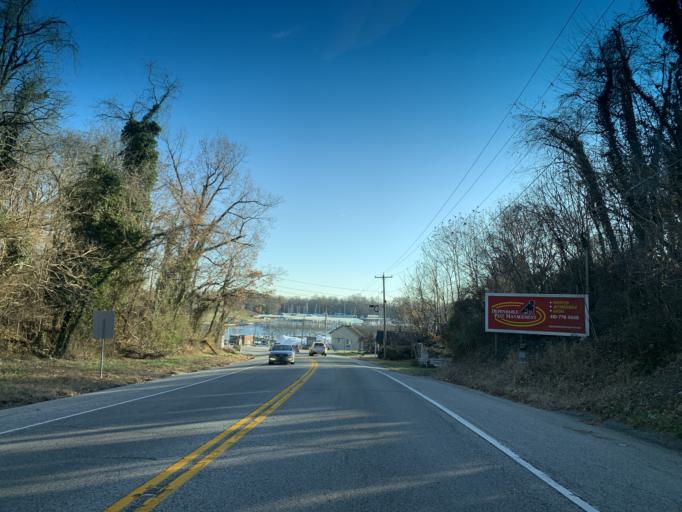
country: US
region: Delaware
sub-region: New Castle County
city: Middletown
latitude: 39.3669
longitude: -75.8838
